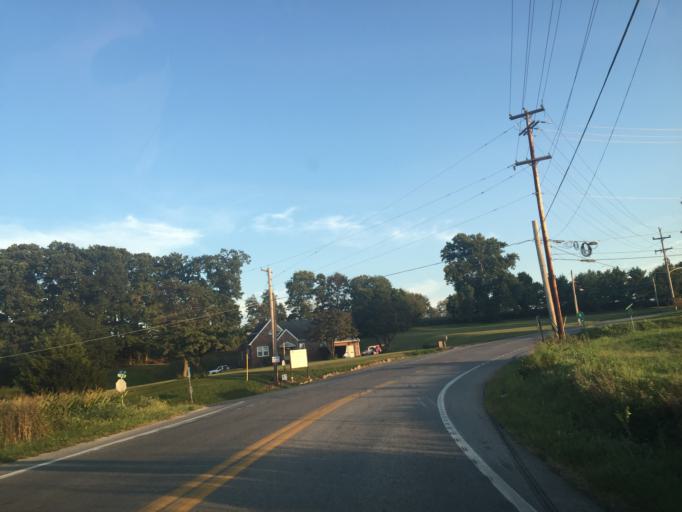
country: US
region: Pennsylvania
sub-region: York County
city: Susquehanna Trails
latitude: 39.7405
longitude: -76.3251
